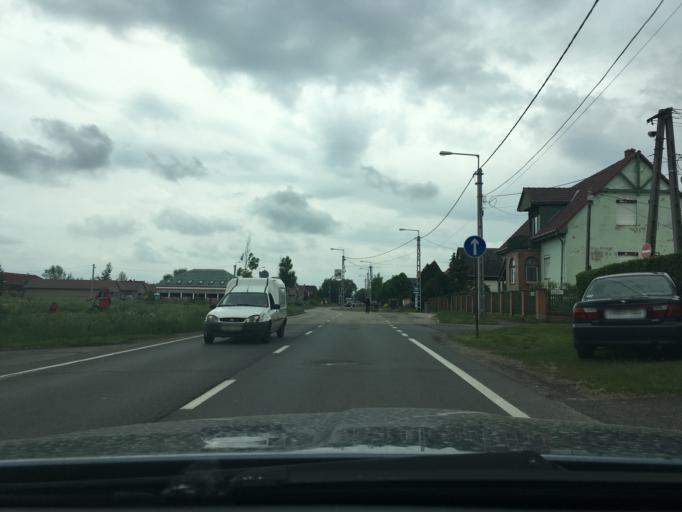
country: HU
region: Hajdu-Bihar
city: Debrecen
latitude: 47.5410
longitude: 21.6713
